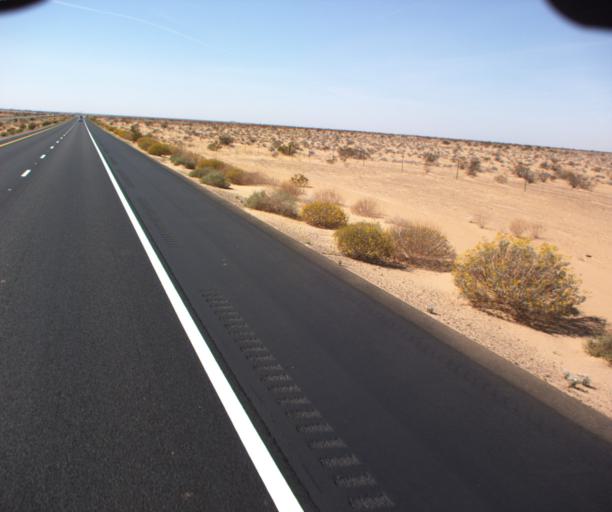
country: US
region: Arizona
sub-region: Yuma County
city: Somerton
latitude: 32.4954
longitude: -114.5999
